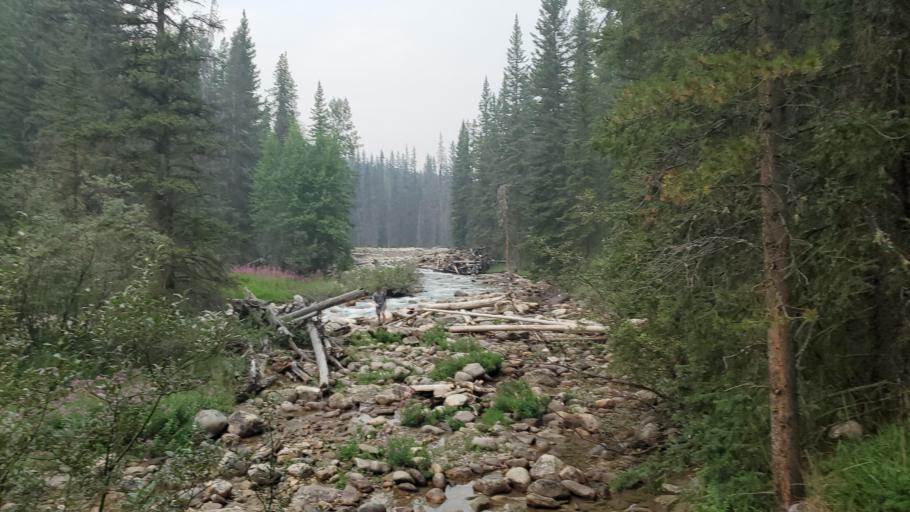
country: CA
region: Alberta
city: Lake Louise
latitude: 51.3495
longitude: -116.0655
